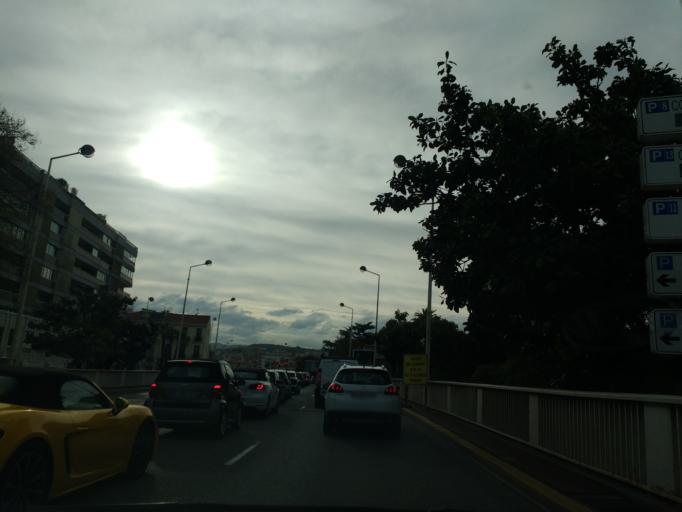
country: FR
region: Provence-Alpes-Cote d'Azur
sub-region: Departement des Alpes-Maritimes
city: Cannes
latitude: 43.5537
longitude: 7.0266
